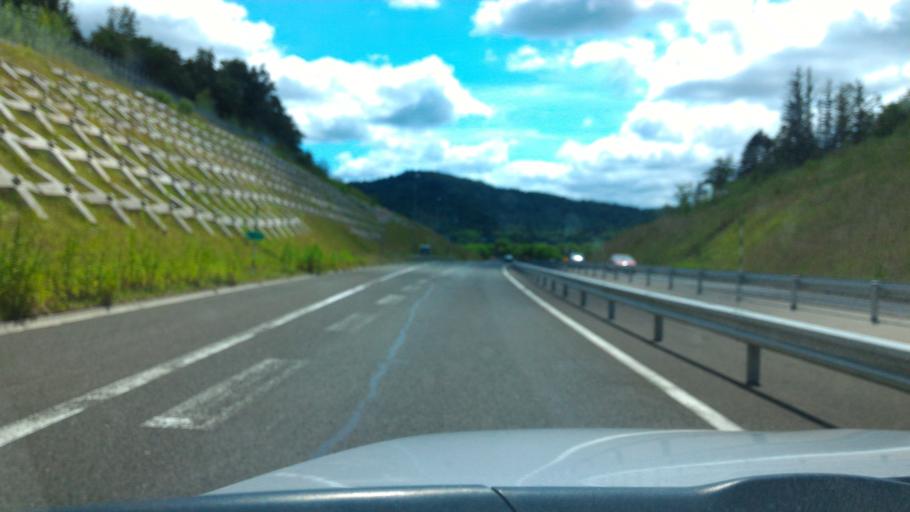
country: JP
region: Hokkaido
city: Shimo-furano
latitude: 42.9833
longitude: 142.4115
